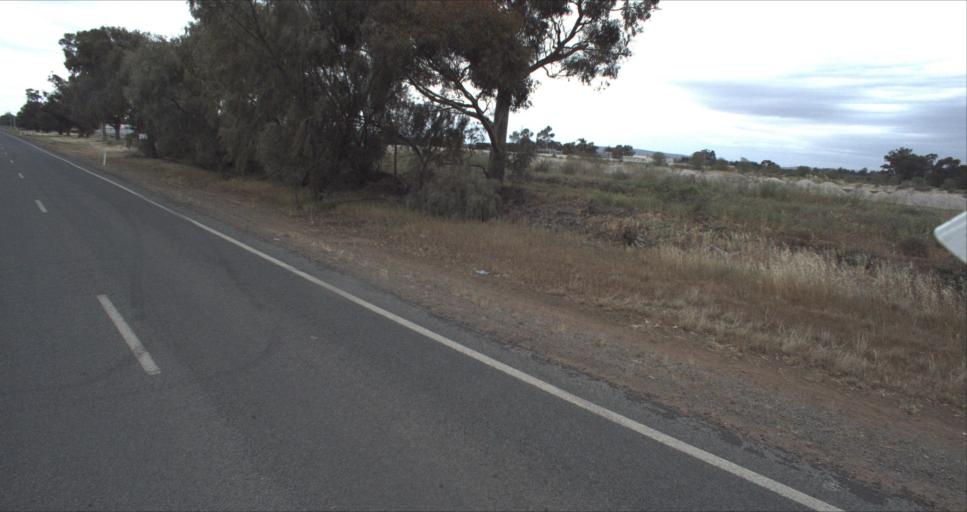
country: AU
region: New South Wales
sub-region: Leeton
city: Leeton
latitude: -34.5420
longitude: 146.3867
